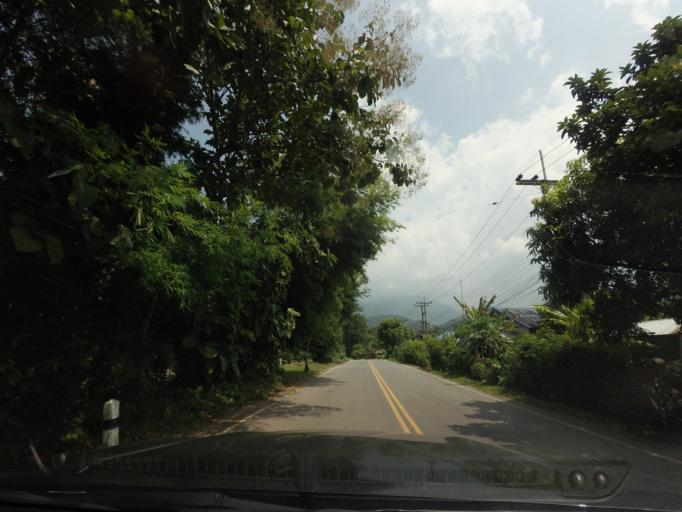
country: TH
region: Nan
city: Santi Suk
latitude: 19.0277
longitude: 100.9321
